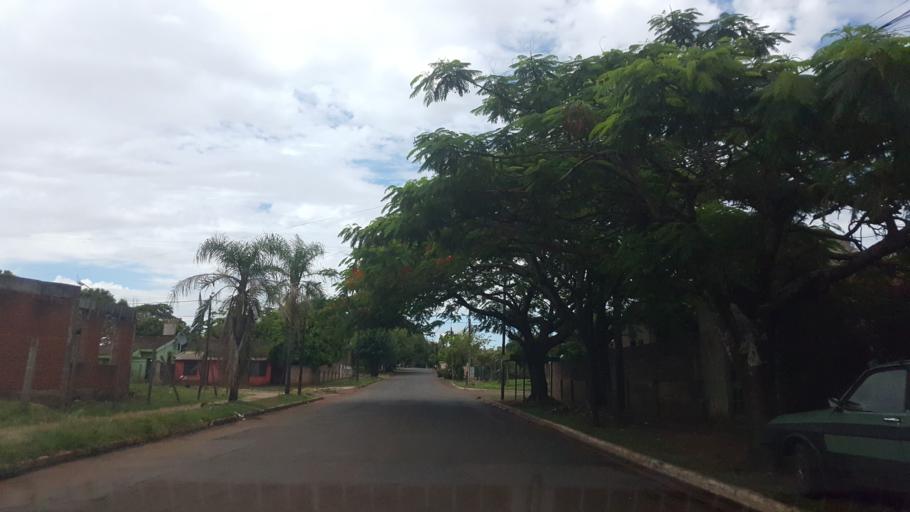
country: AR
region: Misiones
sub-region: Departamento de Capital
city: Posadas
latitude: -27.4221
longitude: -55.8864
